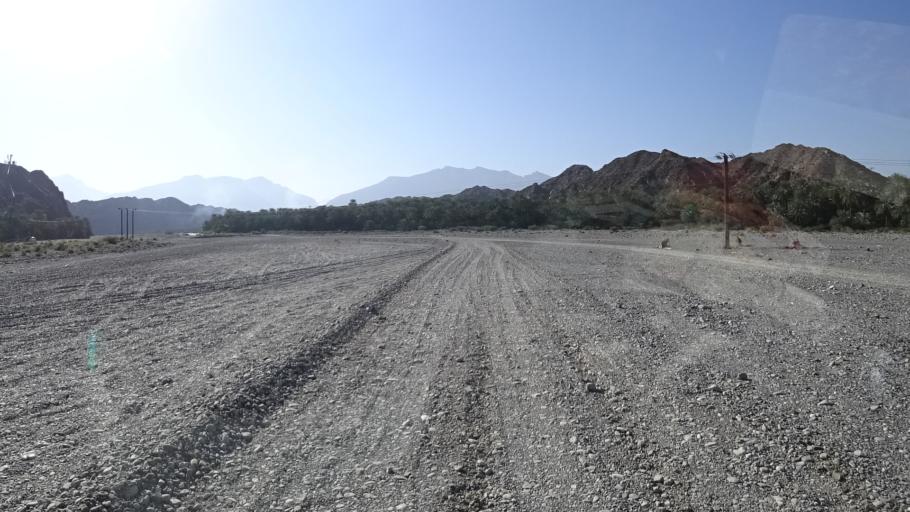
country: OM
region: Al Batinah
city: Bayt al `Awabi
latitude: 23.3876
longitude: 57.6590
